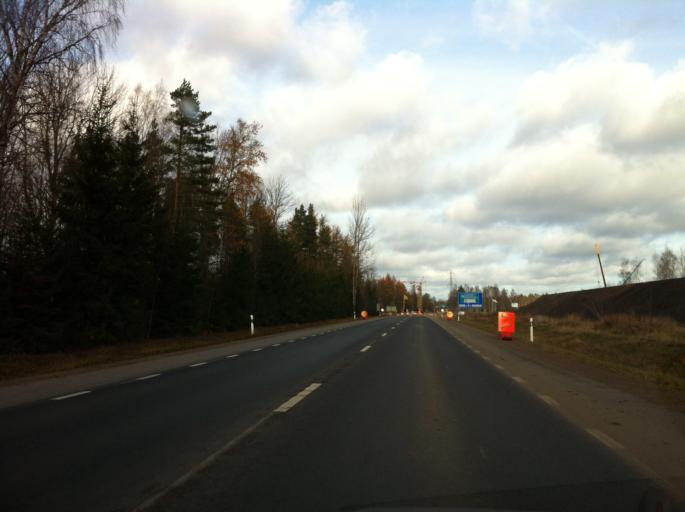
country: SE
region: Kronoberg
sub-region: Vaxjo Kommun
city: Gemla
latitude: 56.8027
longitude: 14.6491
